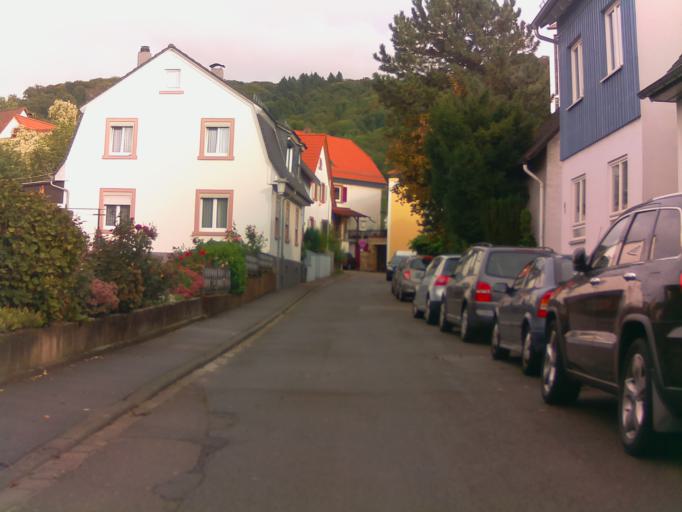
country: DE
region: Baden-Wuerttemberg
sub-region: Karlsruhe Region
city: Weinheim
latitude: 49.5202
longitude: 8.6672
